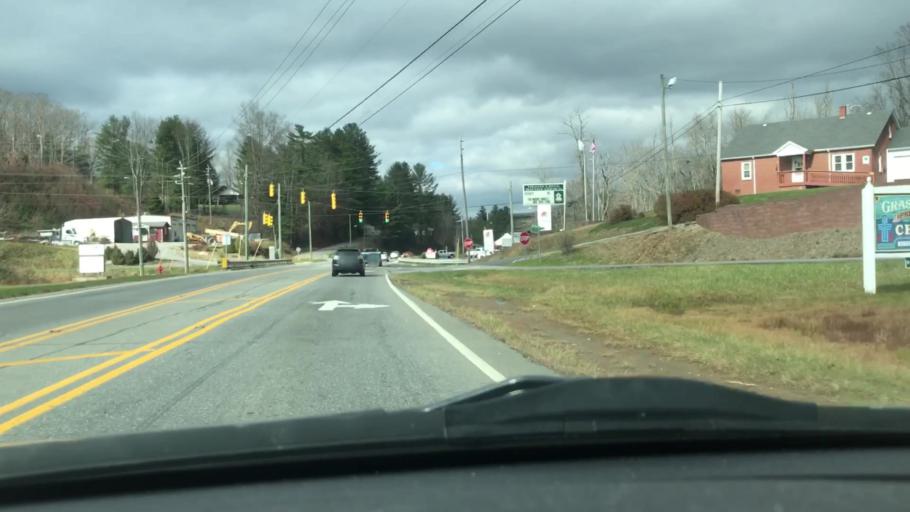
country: US
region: North Carolina
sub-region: Mitchell County
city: Spruce Pine
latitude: 35.8818
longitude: -82.0568
